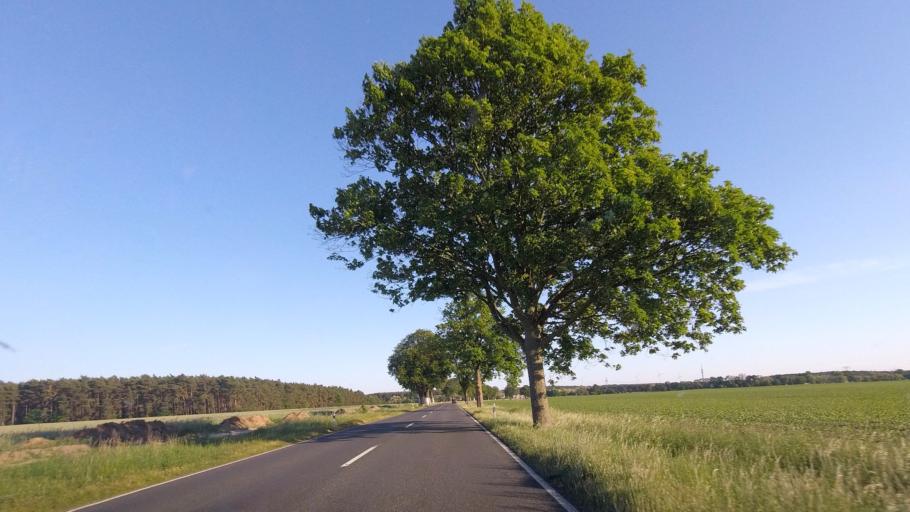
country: DE
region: Brandenburg
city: Golzow
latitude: 52.3422
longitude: 12.6020
